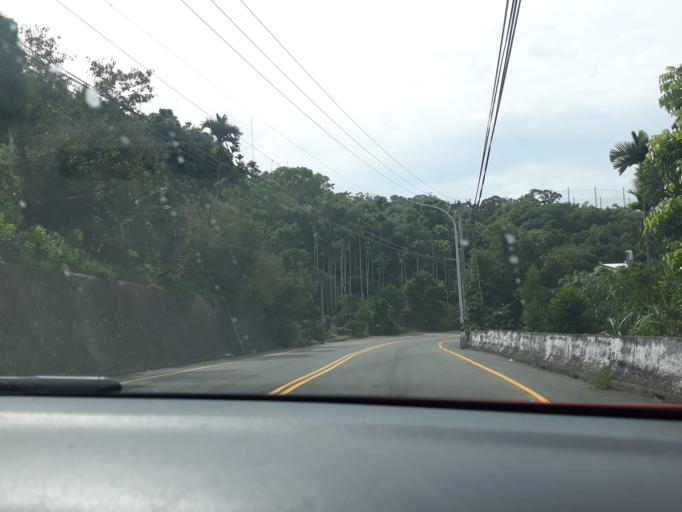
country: TW
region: Taiwan
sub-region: Miaoli
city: Miaoli
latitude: 24.5522
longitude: 120.8047
